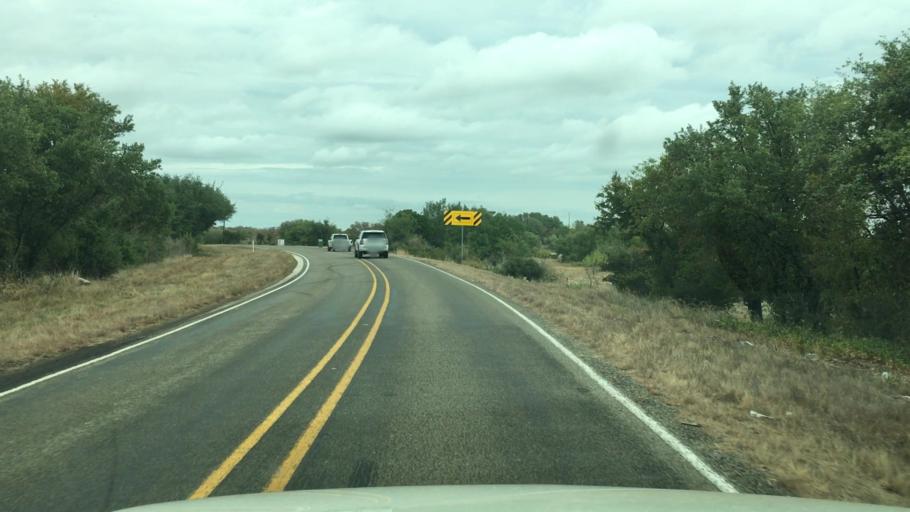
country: US
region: Texas
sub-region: Llano County
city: Horseshoe Bay
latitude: 30.4770
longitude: -98.4172
